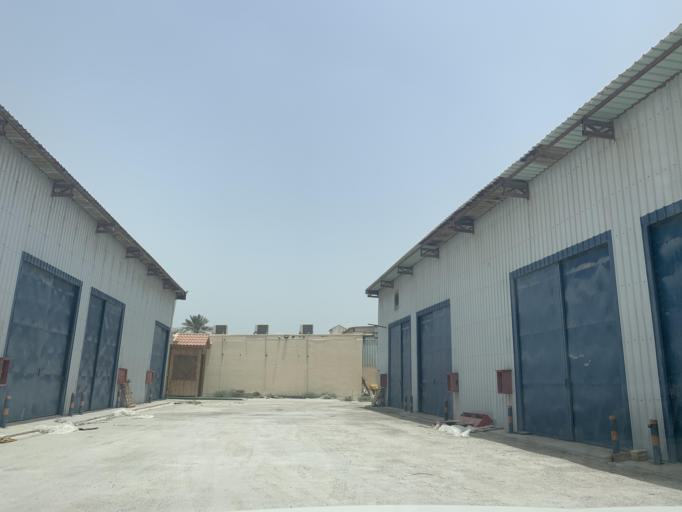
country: BH
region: Manama
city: Jidd Hafs
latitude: 26.2114
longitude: 50.5400
